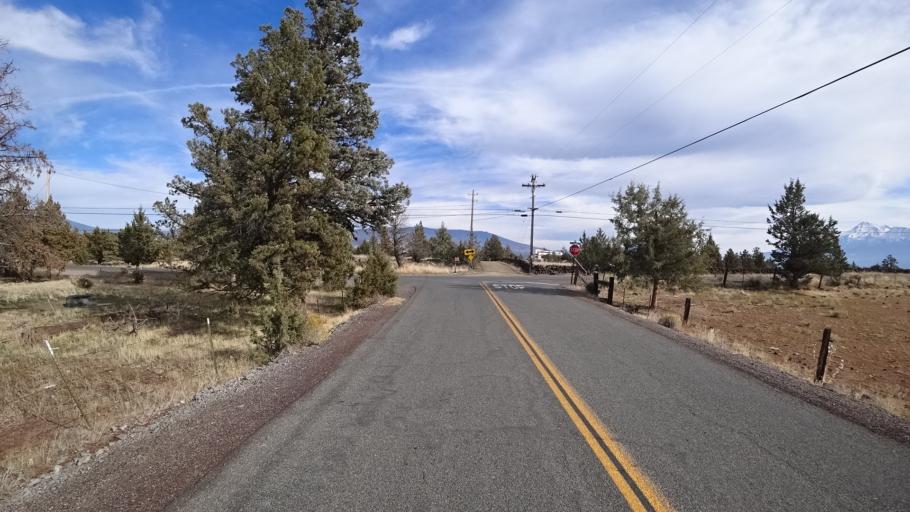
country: US
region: California
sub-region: Siskiyou County
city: Montague
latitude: 41.6383
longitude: -122.3998
